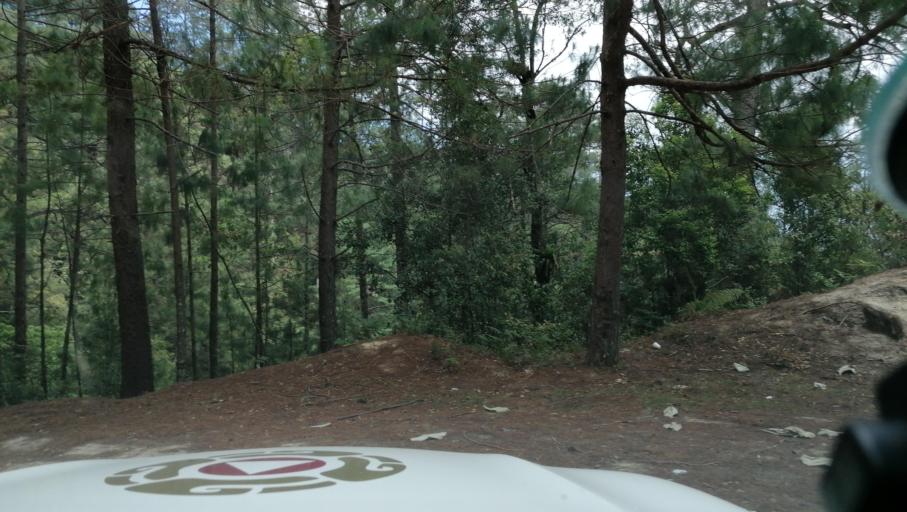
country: MX
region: Chiapas
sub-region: Tapachula
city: Canton Villaflor
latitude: 15.2029
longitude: -92.2322
